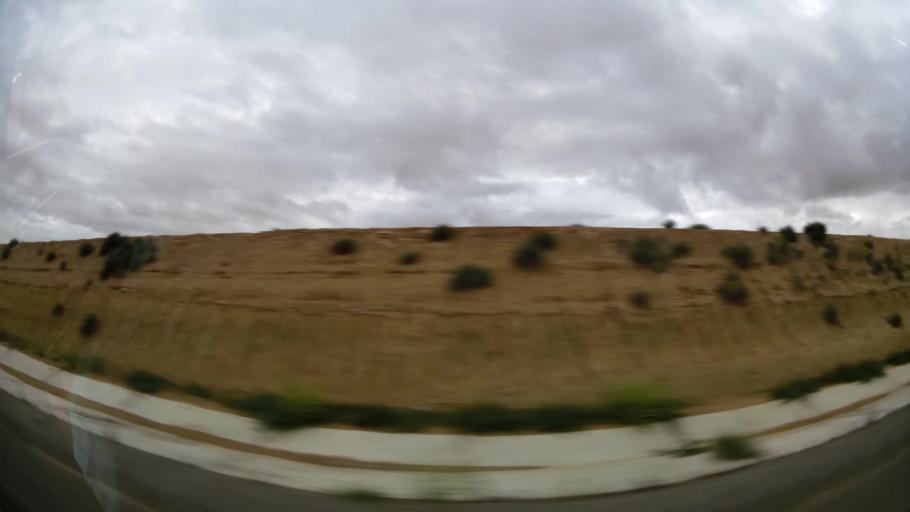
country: MA
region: Taza-Al Hoceima-Taounate
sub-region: Taza
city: Guercif
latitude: 34.3047
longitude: -3.6566
